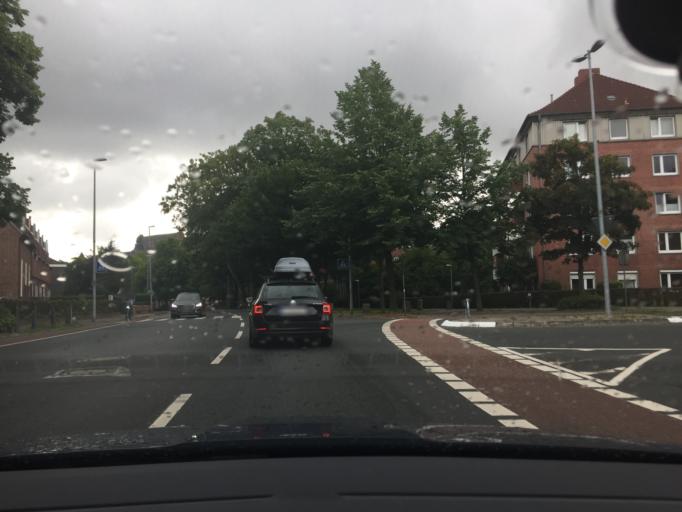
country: DE
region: Lower Saxony
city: Emden
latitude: 53.3664
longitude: 7.1992
